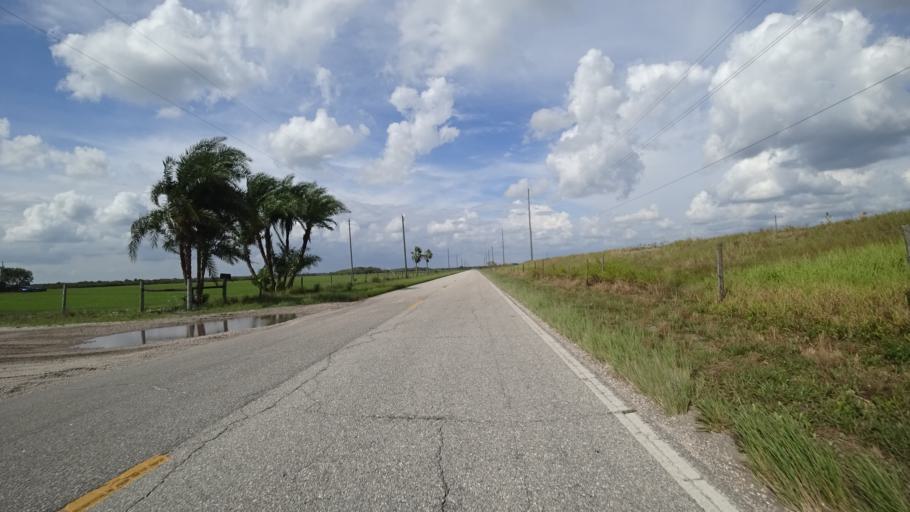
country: US
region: Florida
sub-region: Hardee County
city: Wauchula
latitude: 27.5274
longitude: -82.0759
